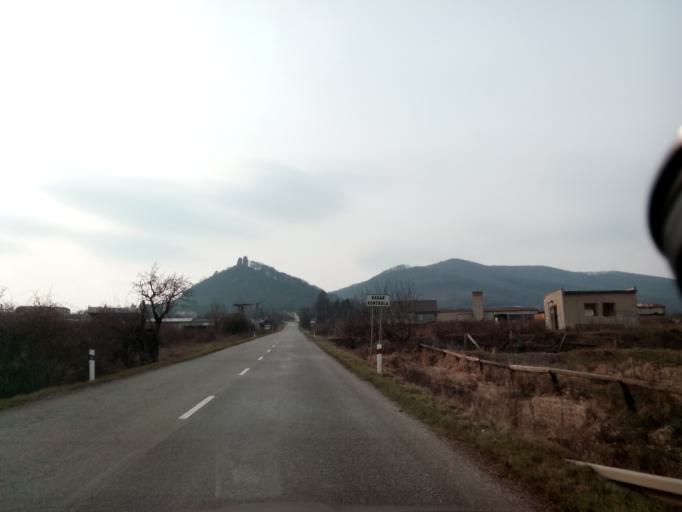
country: SK
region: Kosicky
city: Secovce
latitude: 48.6365
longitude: 21.4884
